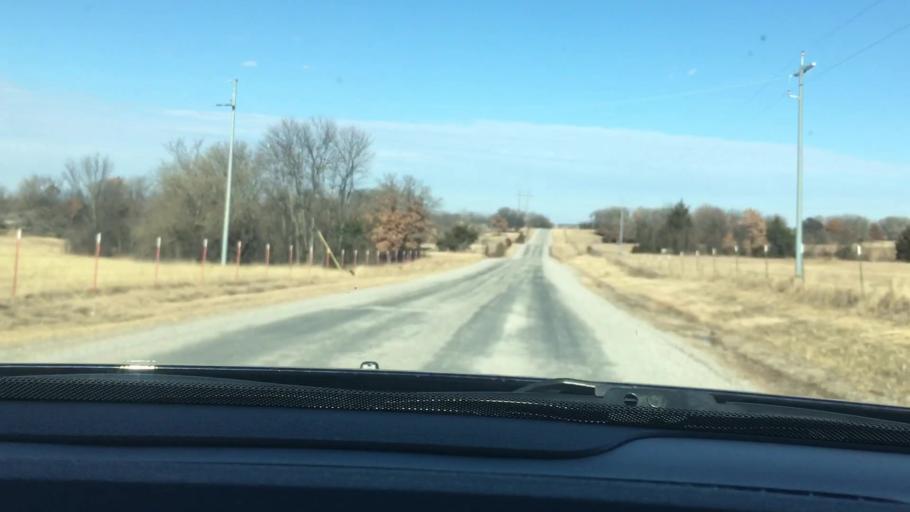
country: US
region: Oklahoma
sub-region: Garvin County
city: Wynnewood
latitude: 34.6573
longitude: -97.0902
